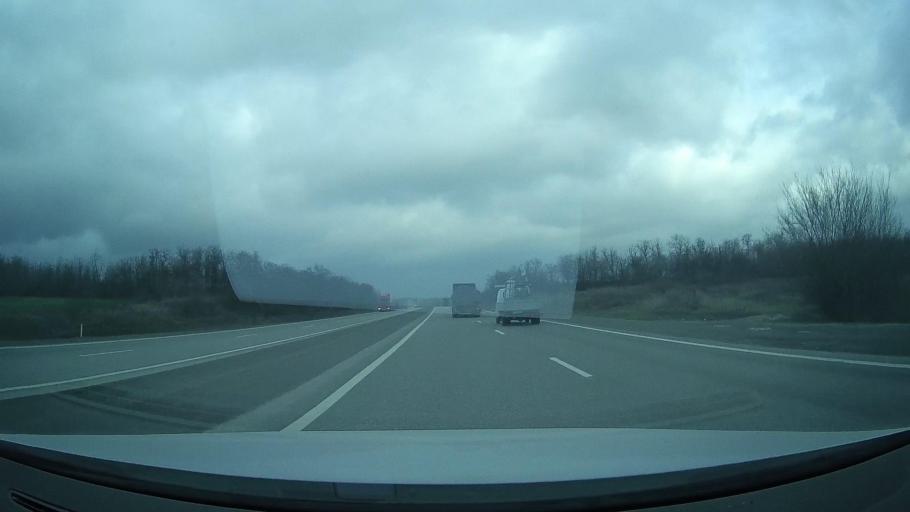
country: RU
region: Rostov
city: Grushevskaya
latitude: 47.5200
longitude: 39.9708
